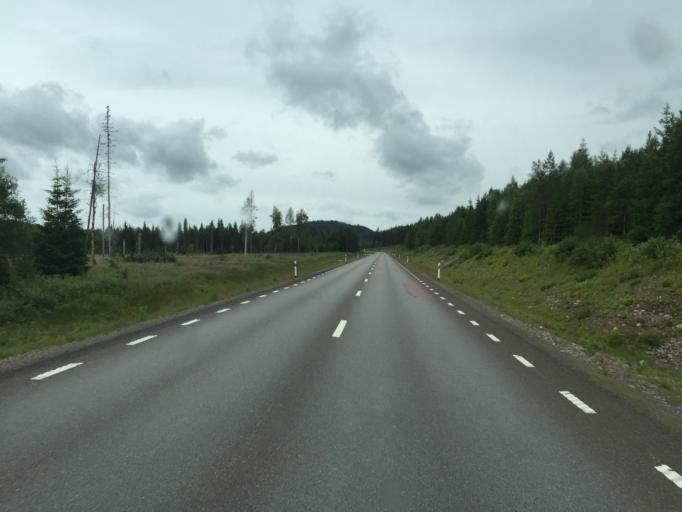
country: SE
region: Dalarna
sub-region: Malung-Saelens kommun
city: Malung
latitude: 60.6275
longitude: 13.6129
